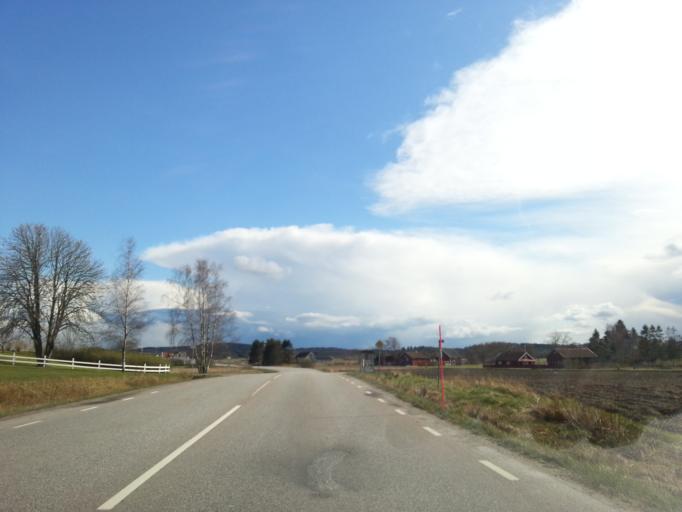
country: SE
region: Vaestra Goetaland
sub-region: Kungalvs Kommun
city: Kode
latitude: 57.9148
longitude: 11.9186
